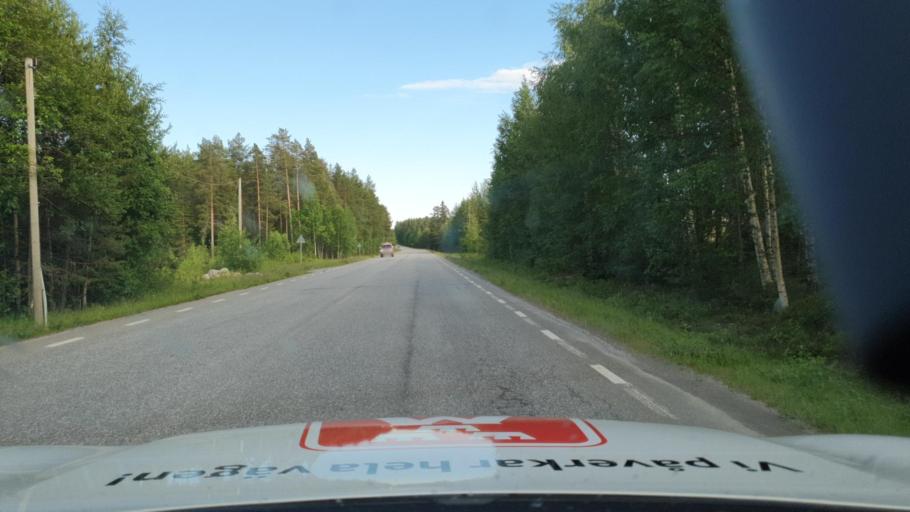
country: SE
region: Vaesterbotten
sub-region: Umea Kommun
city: Roback
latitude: 63.8548
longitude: 20.1483
